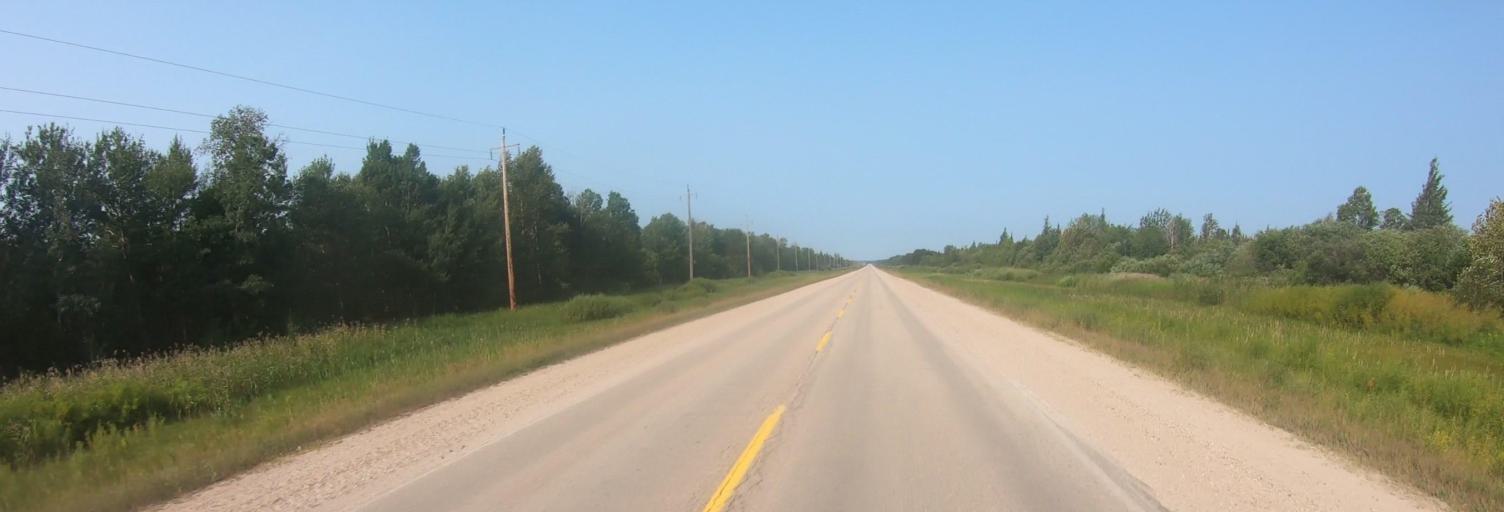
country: US
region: Minnesota
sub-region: Roseau County
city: Roseau
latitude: 49.0235
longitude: -95.6635
